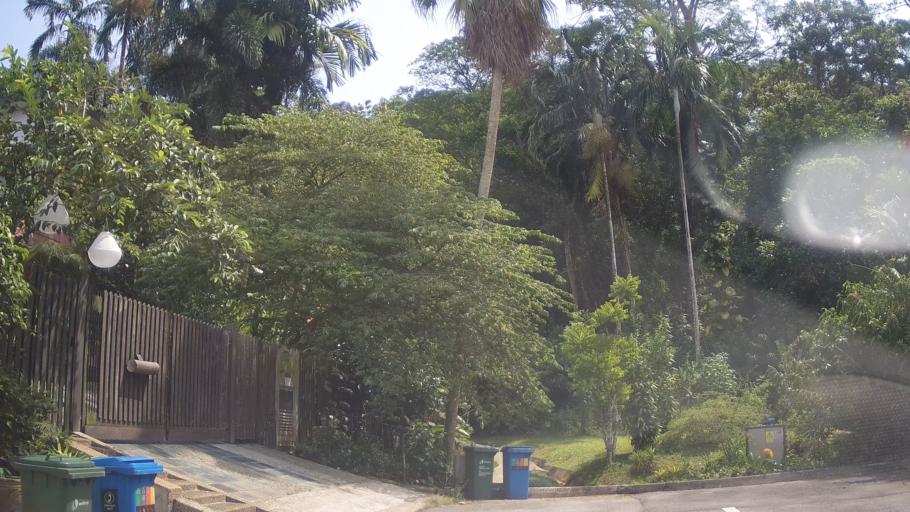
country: MY
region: Johor
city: Johor Bahru
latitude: 1.3595
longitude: 103.7690
